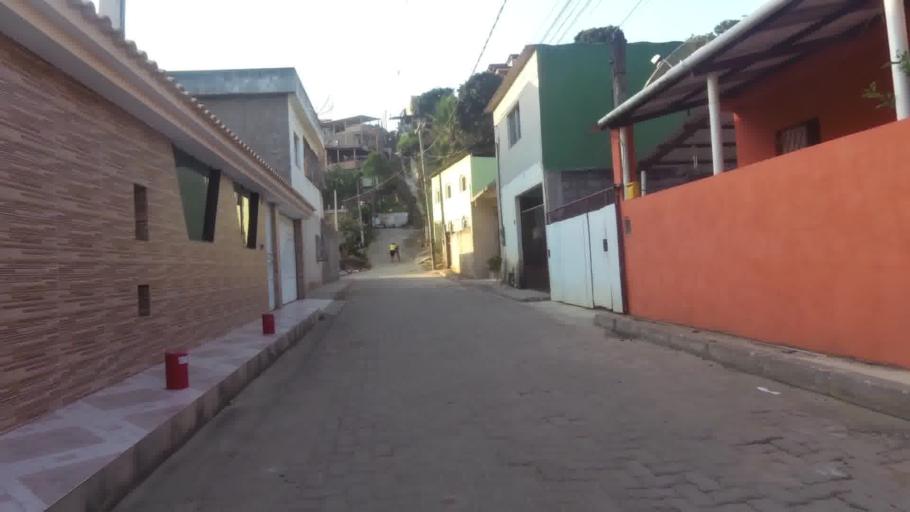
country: BR
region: Espirito Santo
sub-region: Piuma
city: Piuma
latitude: -20.8327
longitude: -40.7227
